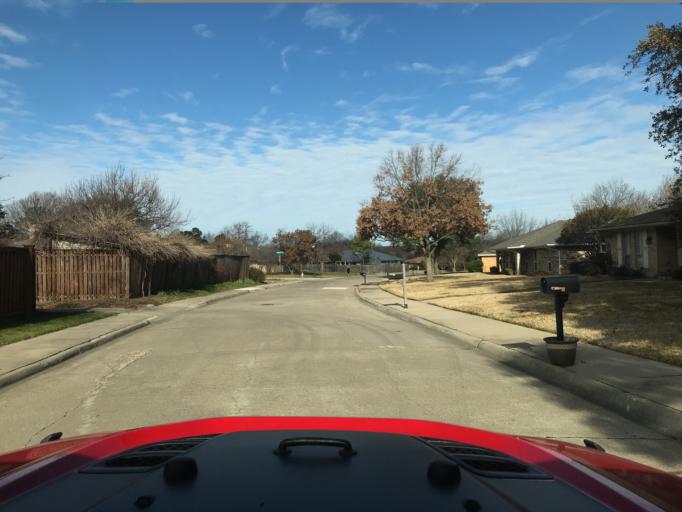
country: US
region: Texas
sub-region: Denton County
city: Lewisville
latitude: 33.0505
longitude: -97.0325
